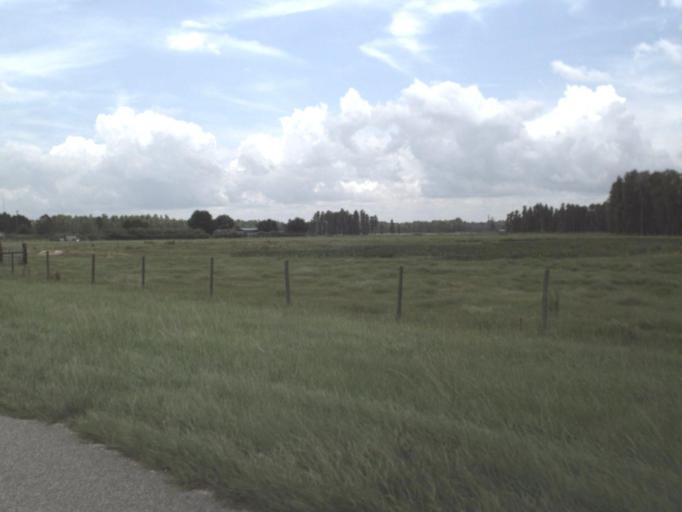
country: US
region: Florida
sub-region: Pasco County
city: Land O' Lakes
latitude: 28.3232
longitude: -82.4124
